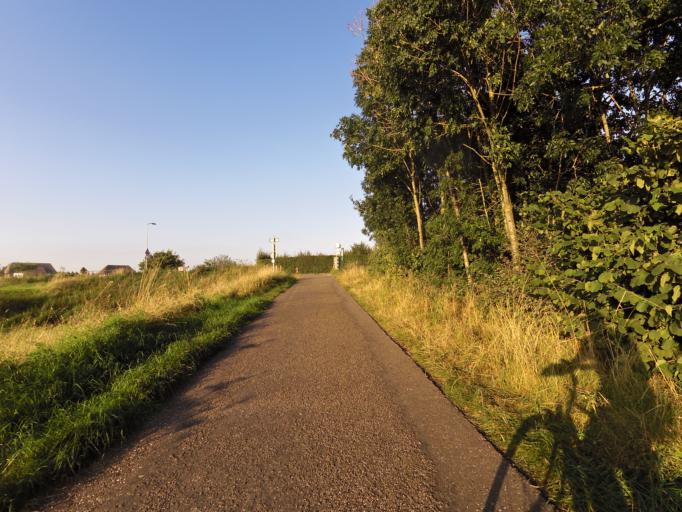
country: NL
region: Gelderland
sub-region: Gemeente Westervoort
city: Westervoort
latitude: 51.9423
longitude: 5.9668
